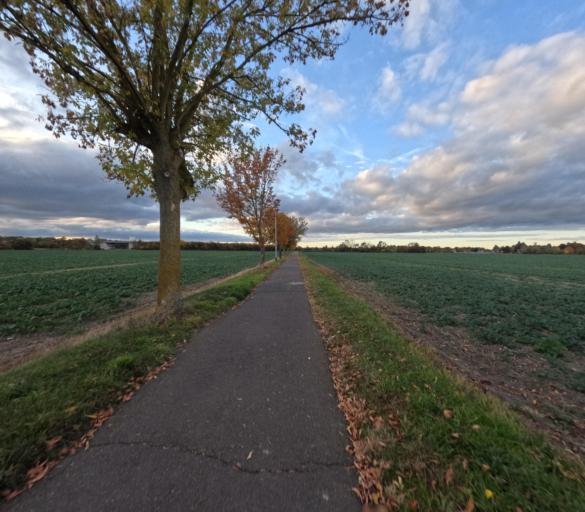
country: DE
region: Saxony
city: Naunhof
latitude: 51.2574
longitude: 12.6270
